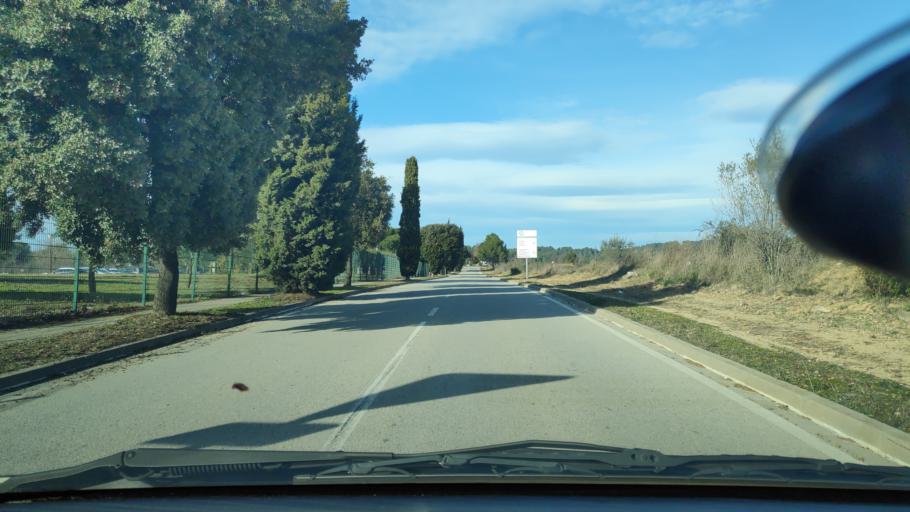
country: ES
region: Catalonia
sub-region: Provincia de Barcelona
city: Sant Cugat del Valles
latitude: 41.4913
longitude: 2.0664
